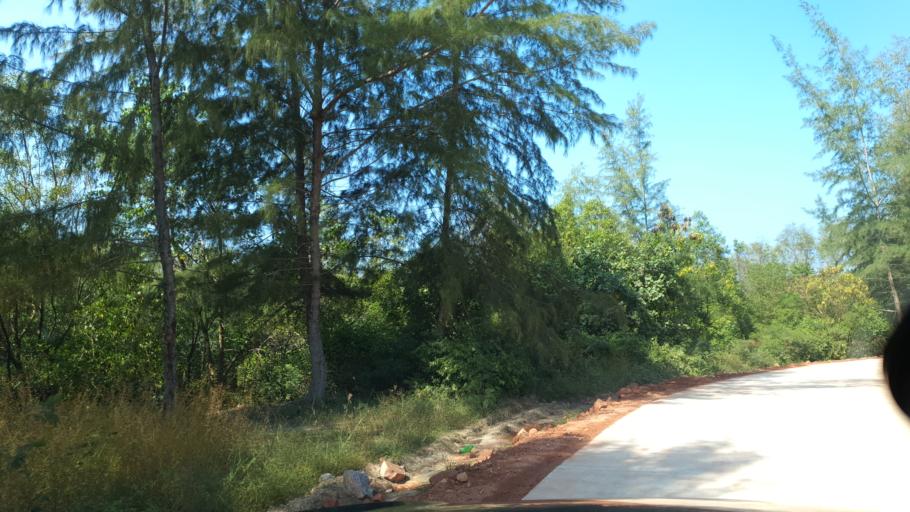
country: TH
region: Surat Thani
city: Tha Chana
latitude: 9.5953
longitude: 99.2087
